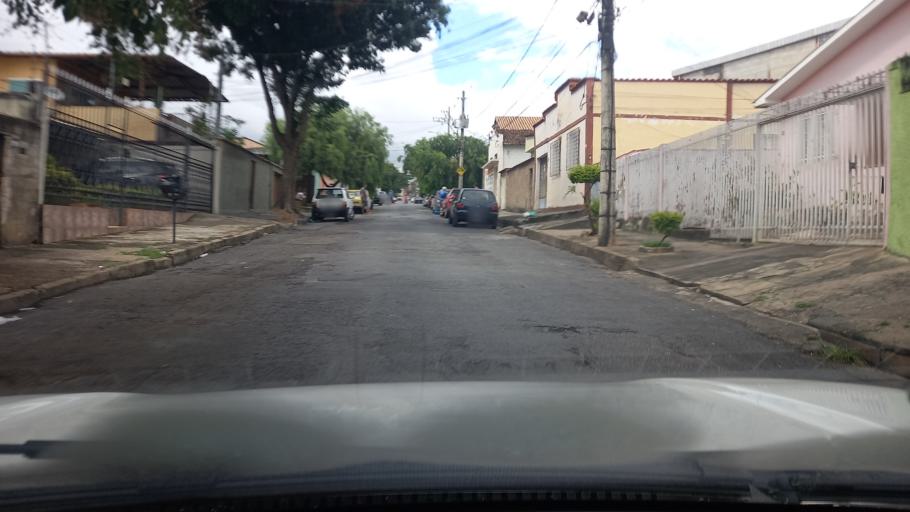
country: BR
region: Minas Gerais
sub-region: Contagem
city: Contagem
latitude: -19.9095
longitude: -44.0028
